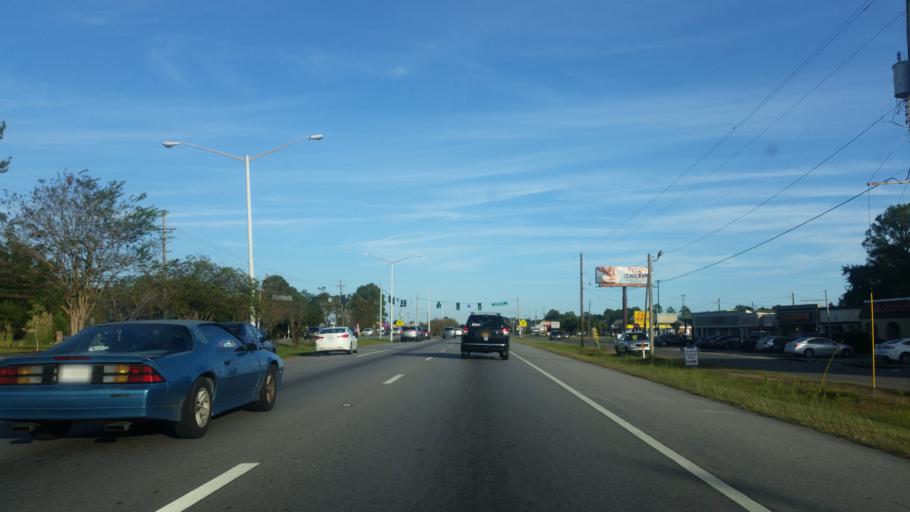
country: US
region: Mississippi
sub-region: Jackson County
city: Ocean Springs
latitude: 30.4143
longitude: -88.7932
